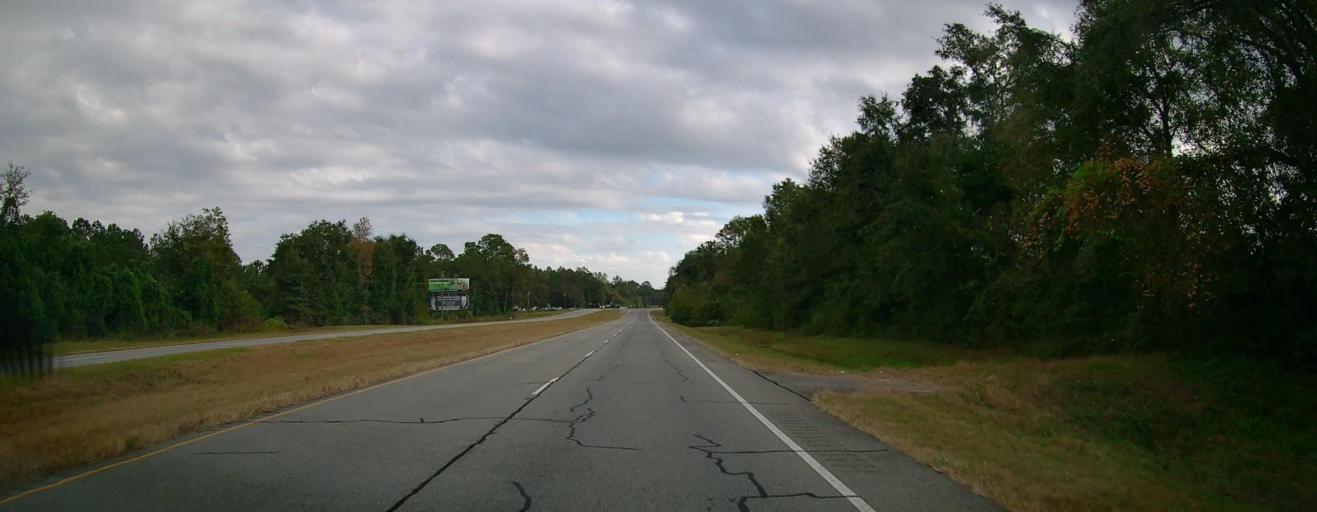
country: US
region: Georgia
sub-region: Thomas County
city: Meigs
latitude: 31.0815
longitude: -84.0838
